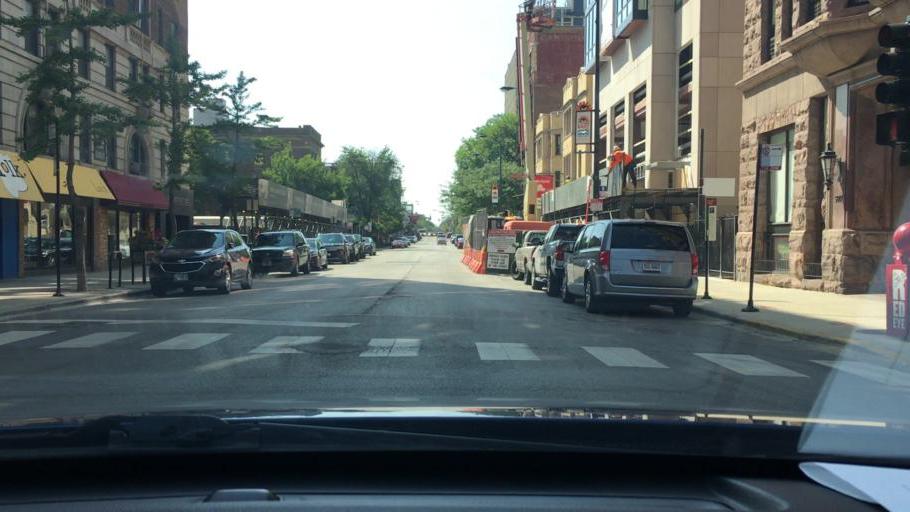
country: US
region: Illinois
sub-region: Cook County
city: Chicago
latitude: 41.9329
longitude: -87.6414
